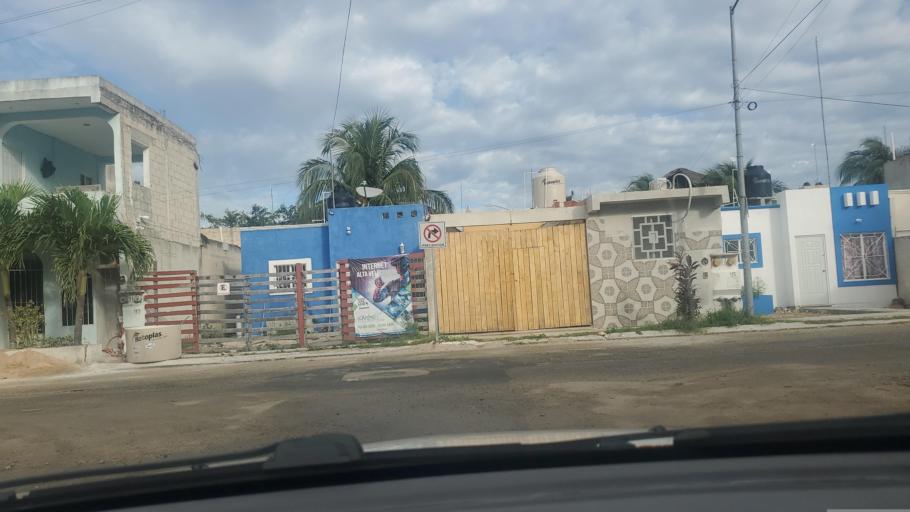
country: MX
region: Quintana Roo
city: Tulum
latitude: 20.2146
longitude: -87.4562
